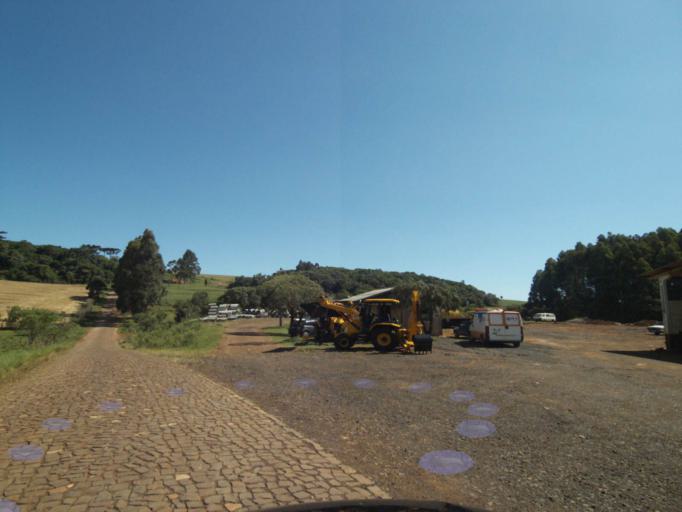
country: BR
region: Parana
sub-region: Coronel Vivida
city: Coronel Vivida
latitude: -26.1474
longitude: -52.3879
